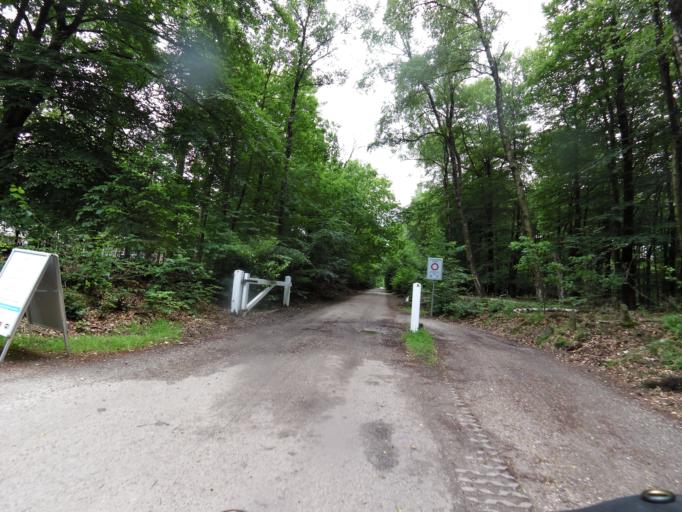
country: NL
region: Gelderland
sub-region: Gemeente Apeldoorn
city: Uddel
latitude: 52.2790
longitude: 5.8047
